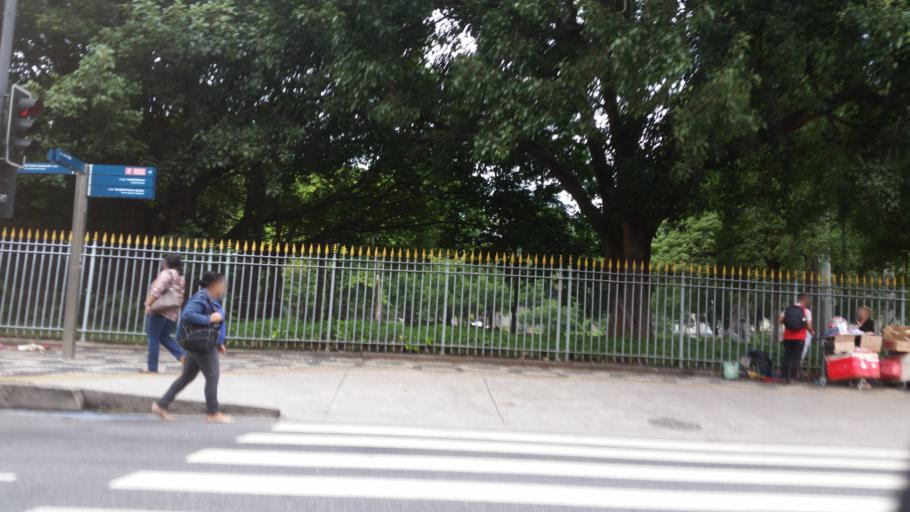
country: BR
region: Rio de Janeiro
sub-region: Rio De Janeiro
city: Rio de Janeiro
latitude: -22.9051
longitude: -43.1903
